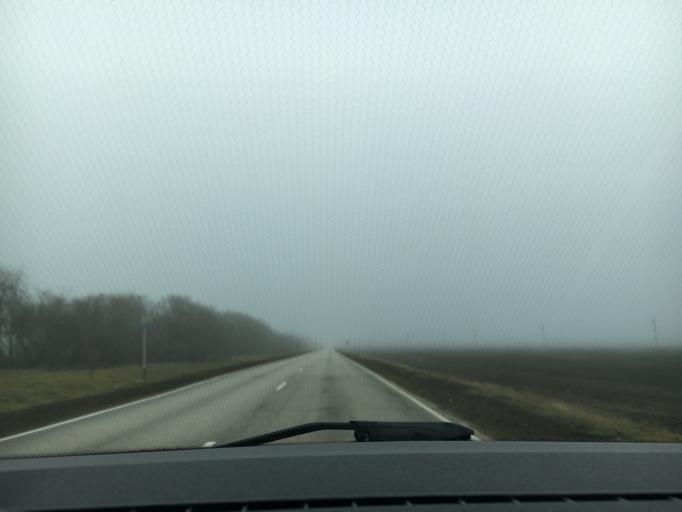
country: RU
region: Rostov
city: Yegorlykskaya
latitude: 46.4156
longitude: 40.7944
